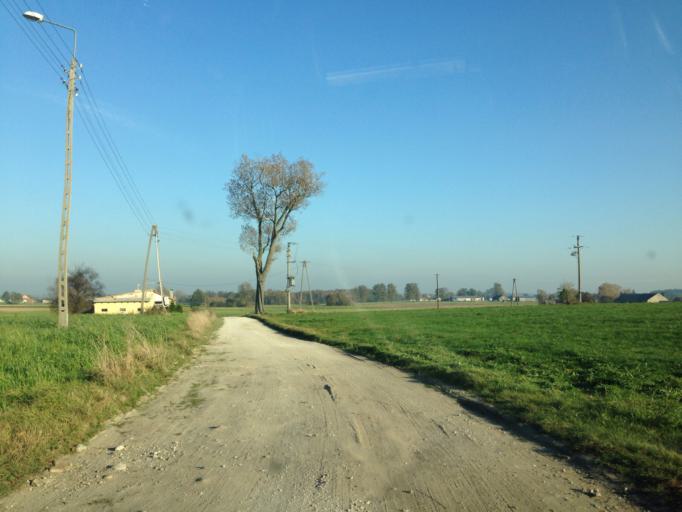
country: PL
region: Kujawsko-Pomorskie
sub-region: Powiat brodnicki
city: Swiedziebnia
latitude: 53.1851
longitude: 19.5609
